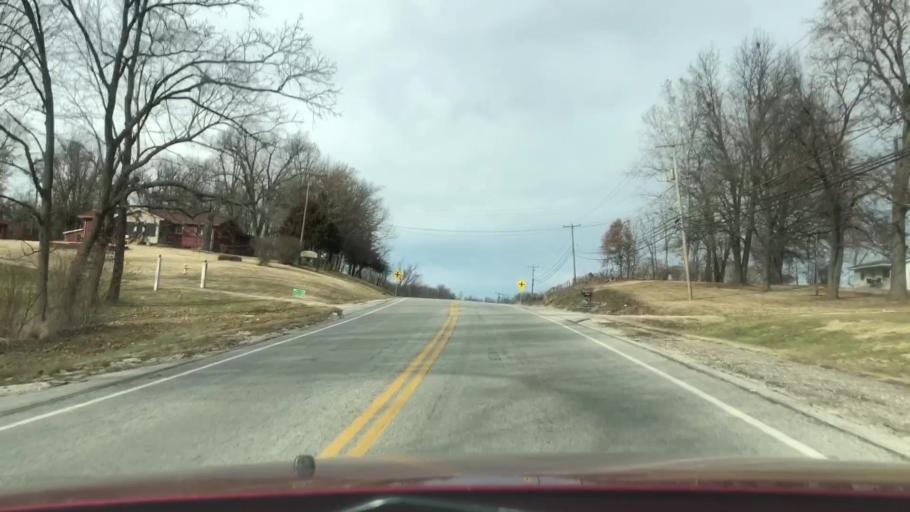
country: US
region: Missouri
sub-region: Greene County
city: Springfield
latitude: 37.2789
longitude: -93.2631
